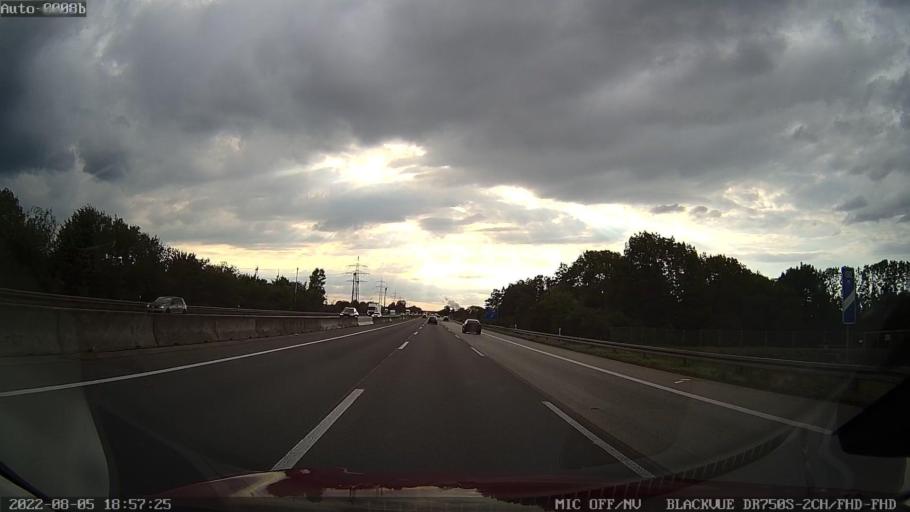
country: DE
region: North Rhine-Westphalia
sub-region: Regierungsbezirk Koln
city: Niederzier
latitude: 50.8361
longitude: 6.4311
